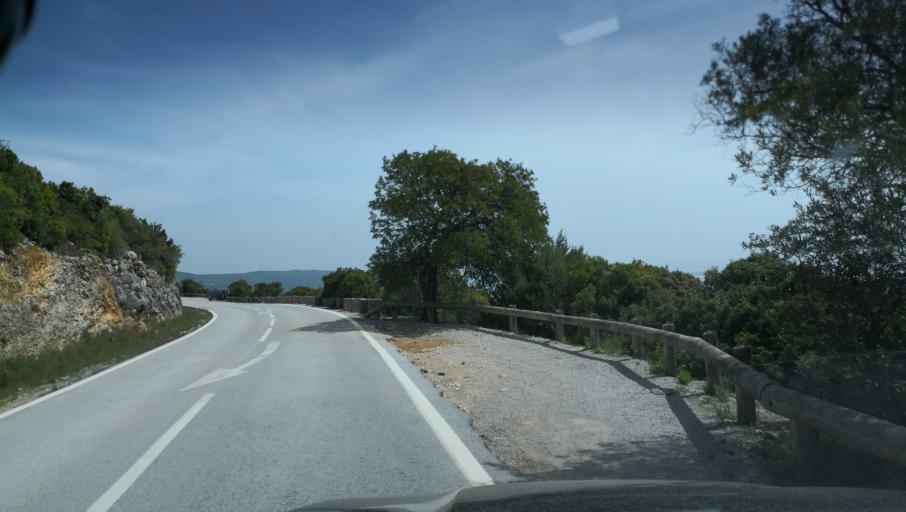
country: PT
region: Setubal
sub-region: Sesimbra
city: Sesimbra
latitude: 38.4633
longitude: -9.0050
